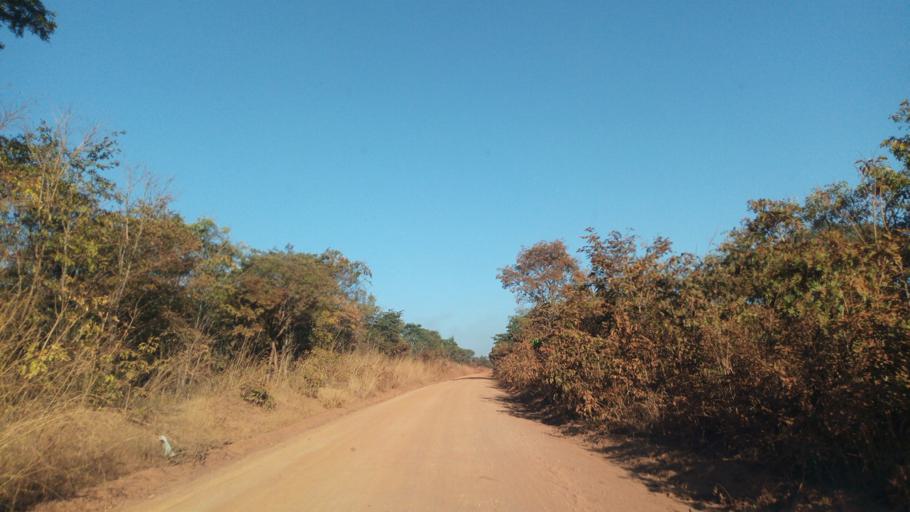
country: ZM
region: Luapula
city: Mwense
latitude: -10.4852
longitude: 28.4968
